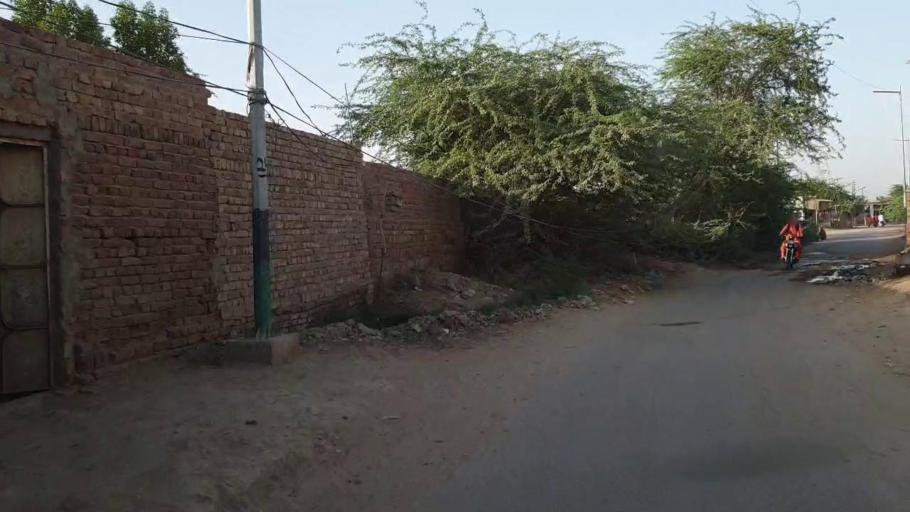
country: PK
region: Sindh
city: Jam Sahib
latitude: 26.2979
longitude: 68.6312
